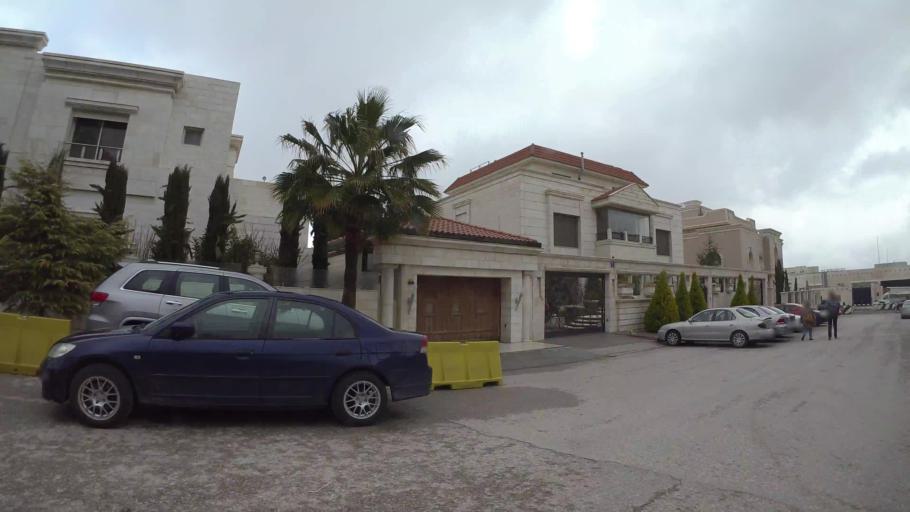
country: JO
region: Amman
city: Al Bunayyat ash Shamaliyah
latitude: 31.9456
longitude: 35.8782
